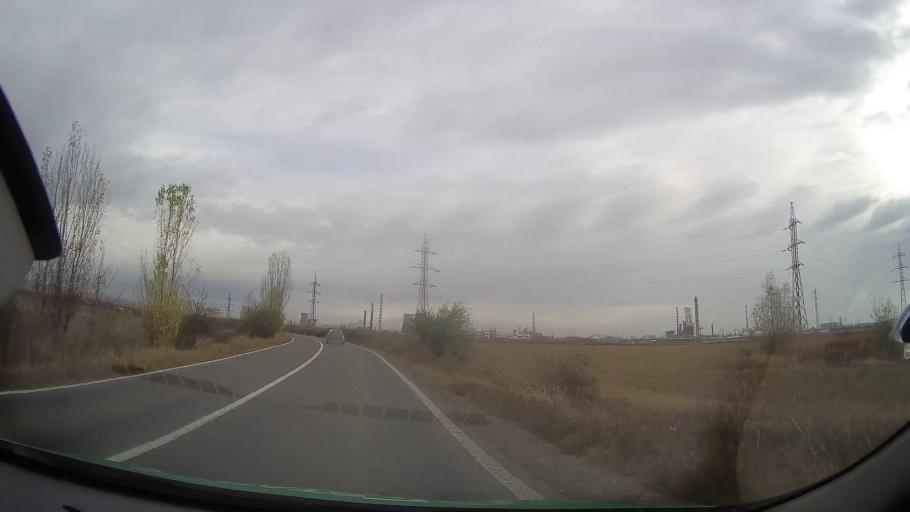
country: RO
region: Prahova
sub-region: Comuna Bucov
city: Bucov
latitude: 44.9525
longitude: 26.0562
